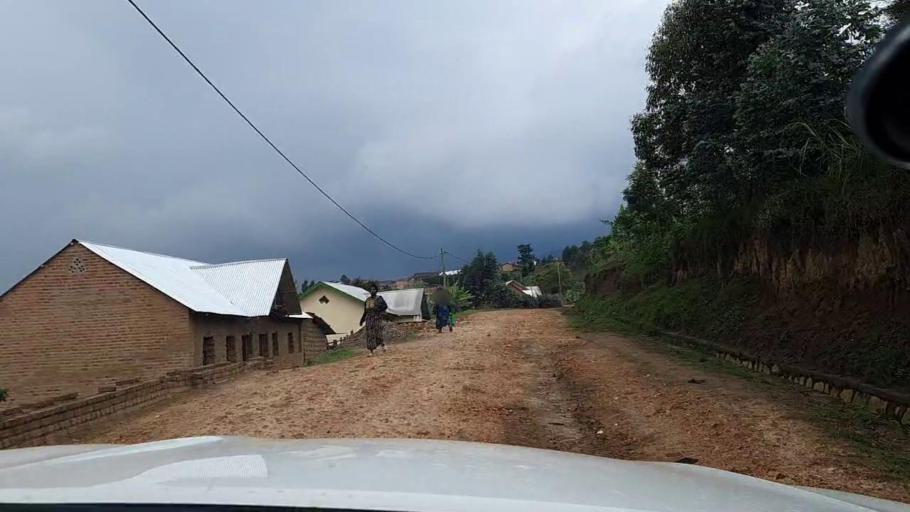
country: RW
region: Western Province
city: Kibuye
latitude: -2.1038
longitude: 29.4847
